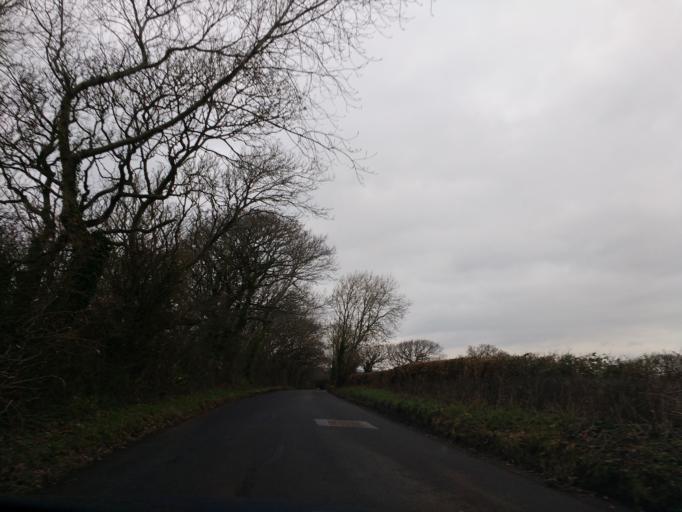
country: GB
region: England
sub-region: Isle of Wight
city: Shalfleet
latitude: 50.6907
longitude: -1.4006
